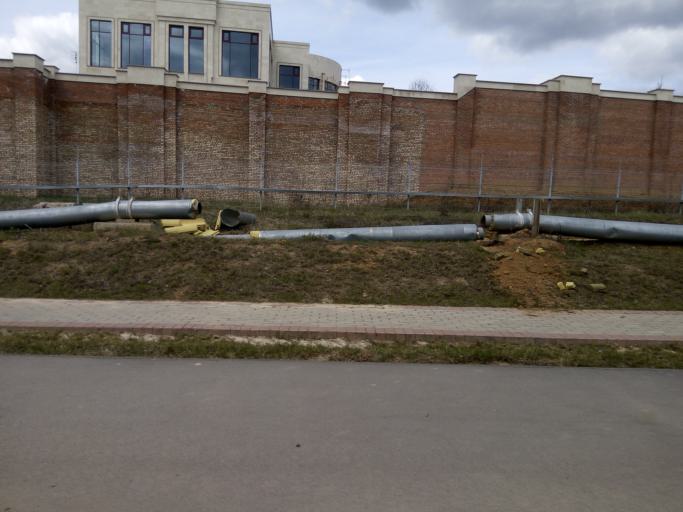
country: RU
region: Moskovskaya
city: Skolkovo
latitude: 55.6839
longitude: 37.3477
